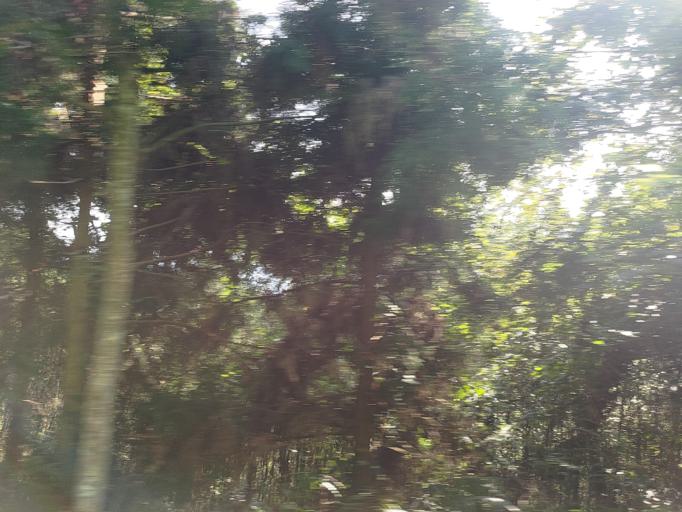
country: TW
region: Taiwan
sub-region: Hsinchu
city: Hsinchu
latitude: 24.6168
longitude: 121.0935
